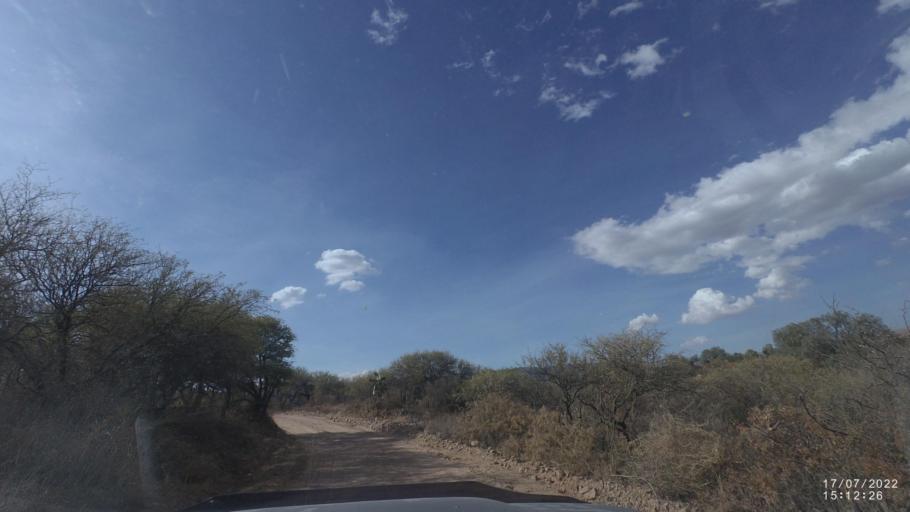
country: BO
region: Cochabamba
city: Capinota
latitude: -17.5701
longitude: -66.2634
